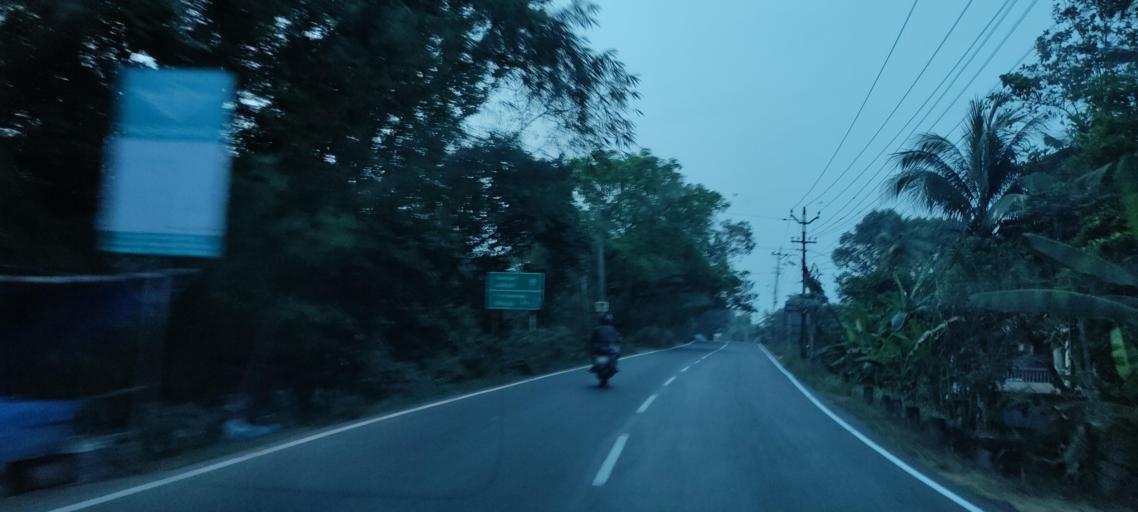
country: IN
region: Kerala
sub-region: Alappuzha
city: Mavelikara
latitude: 9.3298
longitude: 76.4666
